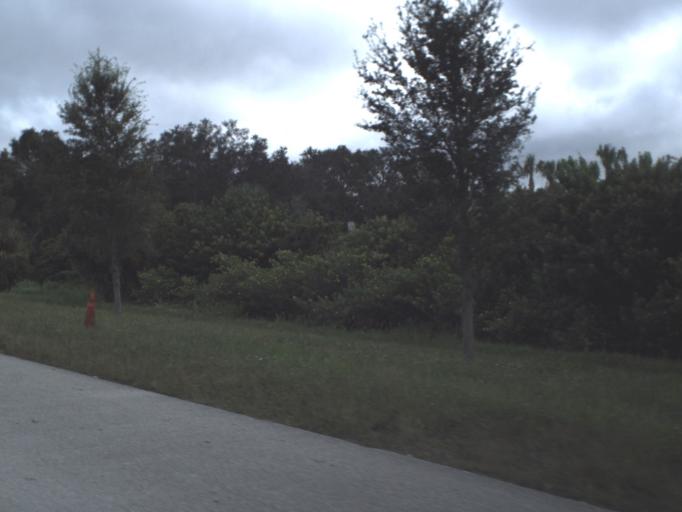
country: US
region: Florida
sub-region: Sarasota County
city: Laurel
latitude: 27.1517
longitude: -82.4615
